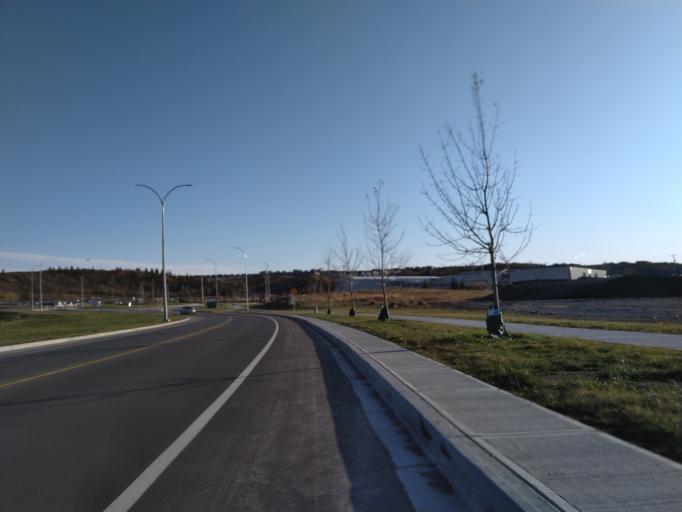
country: CA
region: Alberta
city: Cochrane
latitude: 51.1790
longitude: -114.4514
